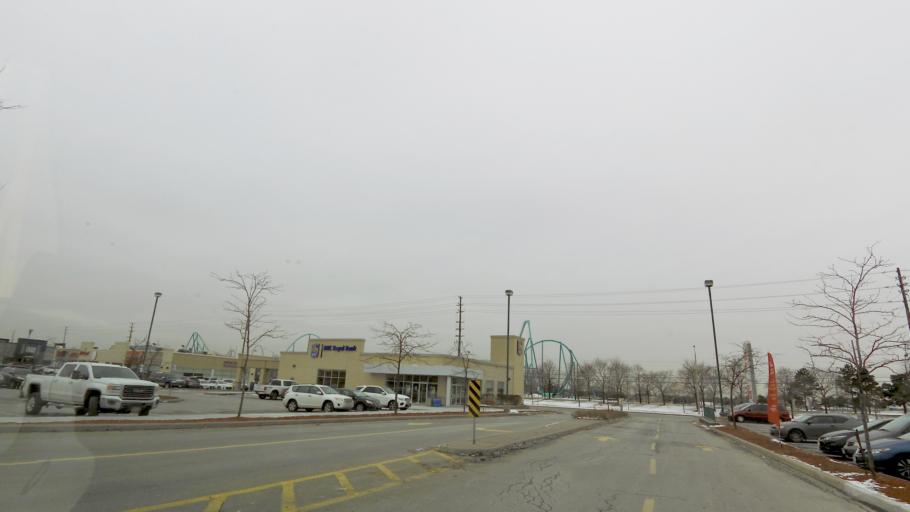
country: CA
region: Ontario
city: Vaughan
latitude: 43.8483
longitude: -79.5353
